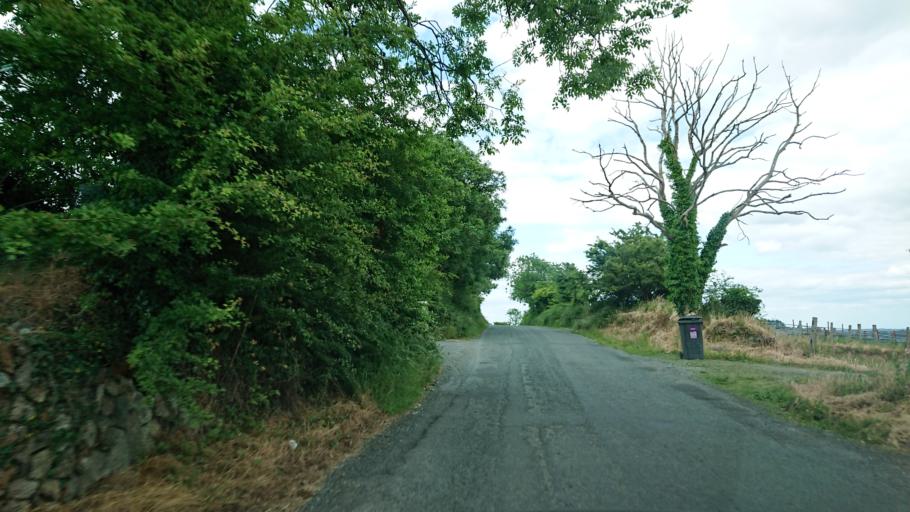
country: IE
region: Munster
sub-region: Waterford
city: Tra Mhor
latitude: 52.2043
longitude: -7.1774
